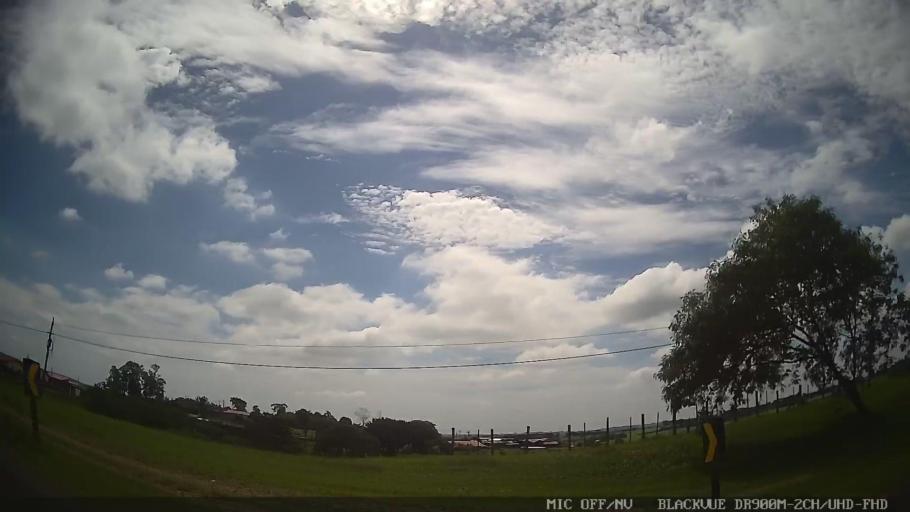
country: BR
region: Sao Paulo
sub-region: Tiete
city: Tiete
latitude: -23.0884
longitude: -47.7794
